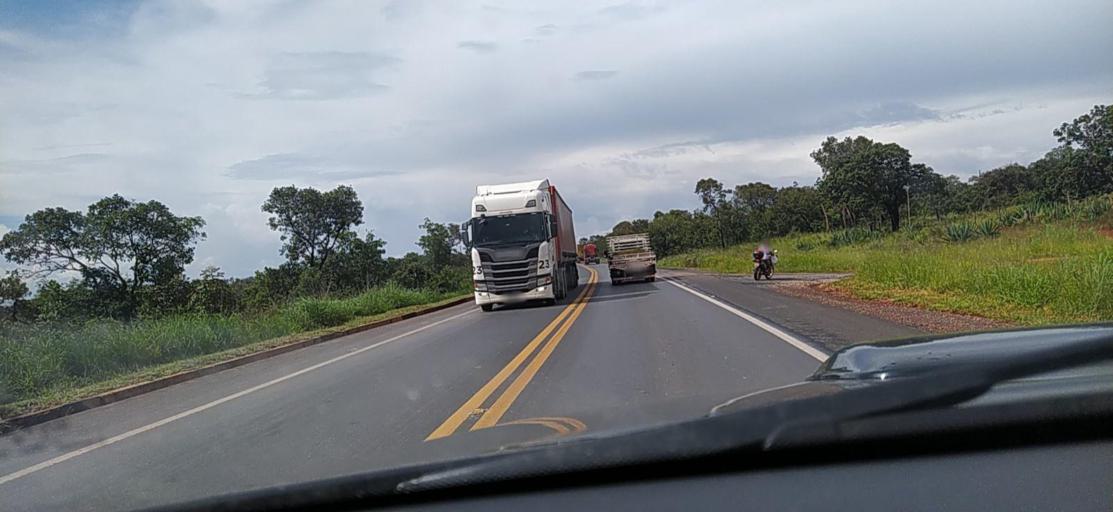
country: BR
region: Minas Gerais
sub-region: Montes Claros
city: Montes Claros
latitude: -16.8676
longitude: -43.8542
